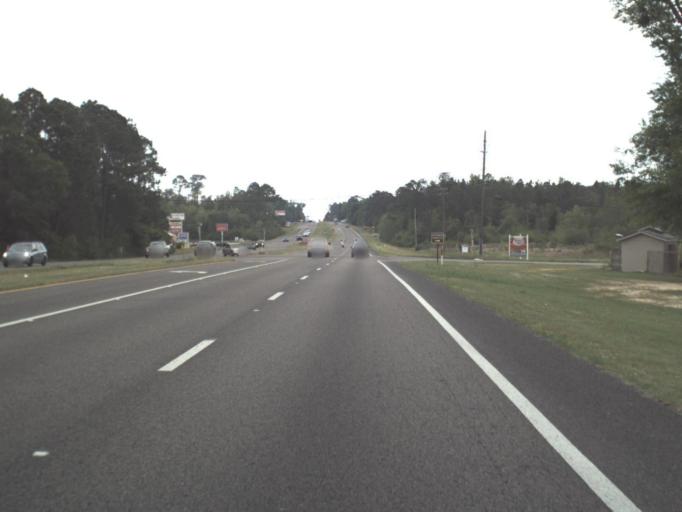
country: US
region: Florida
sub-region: Escambia County
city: Cantonment
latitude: 30.6224
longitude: -87.3275
